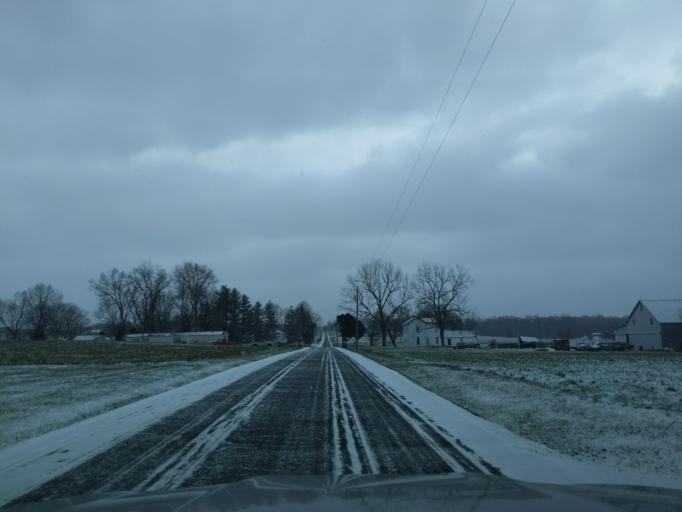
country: US
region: Indiana
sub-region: Decatur County
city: Westport
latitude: 39.2262
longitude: -85.5176
